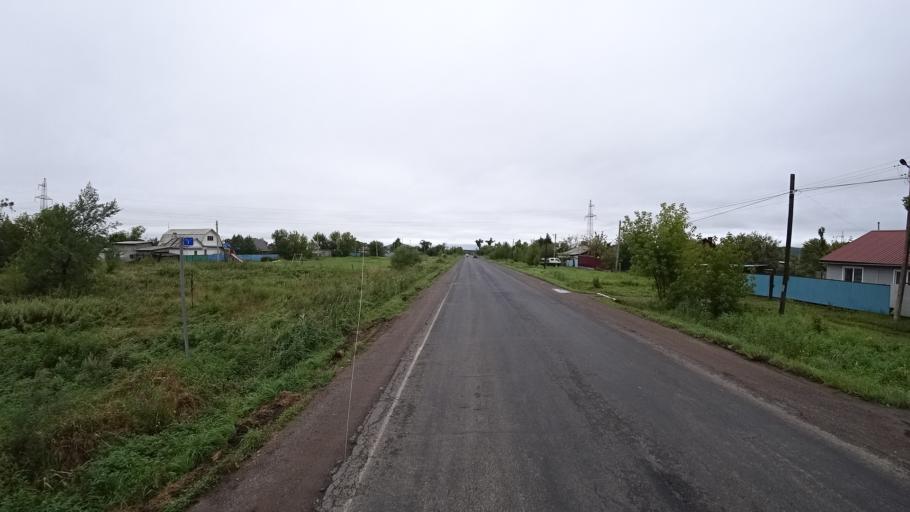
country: RU
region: Primorskiy
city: Monastyrishche
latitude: 44.1992
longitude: 132.4772
